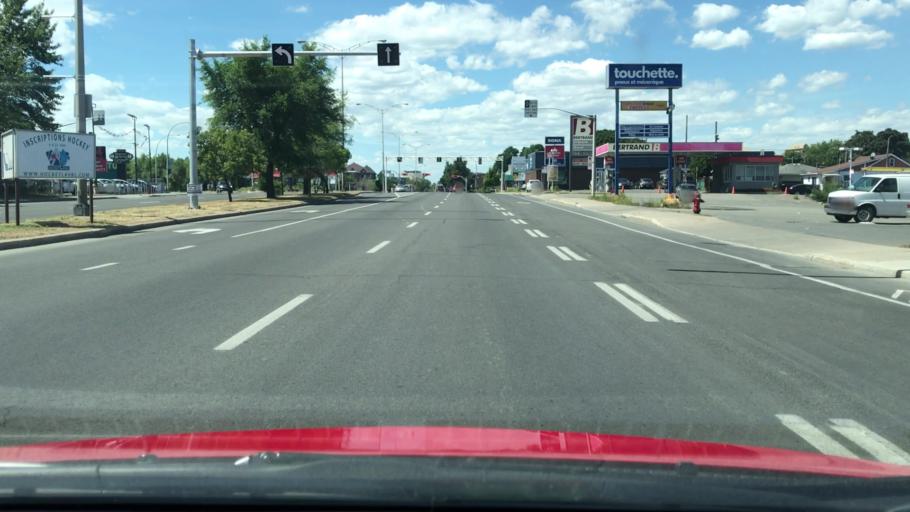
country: CA
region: Quebec
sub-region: Laval
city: Laval
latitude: 45.5374
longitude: -73.7322
